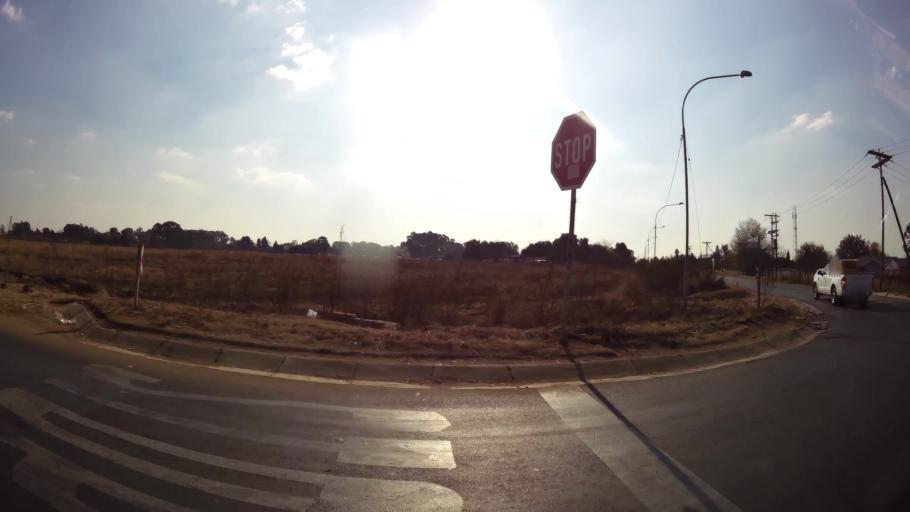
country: ZA
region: Gauteng
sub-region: Ekurhuleni Metropolitan Municipality
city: Benoni
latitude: -26.1247
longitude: 28.3931
